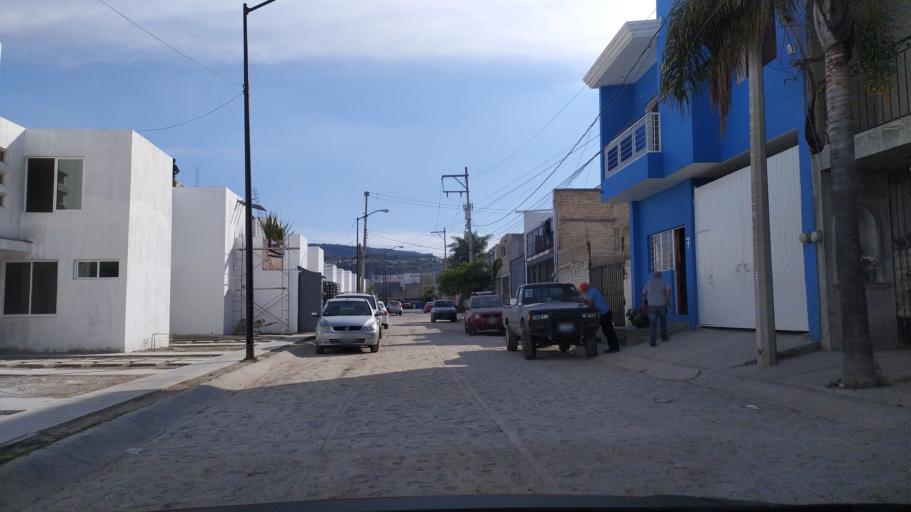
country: MX
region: Jalisco
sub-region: Tlajomulco de Zuniga
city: Palomar
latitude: 20.6316
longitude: -103.4714
